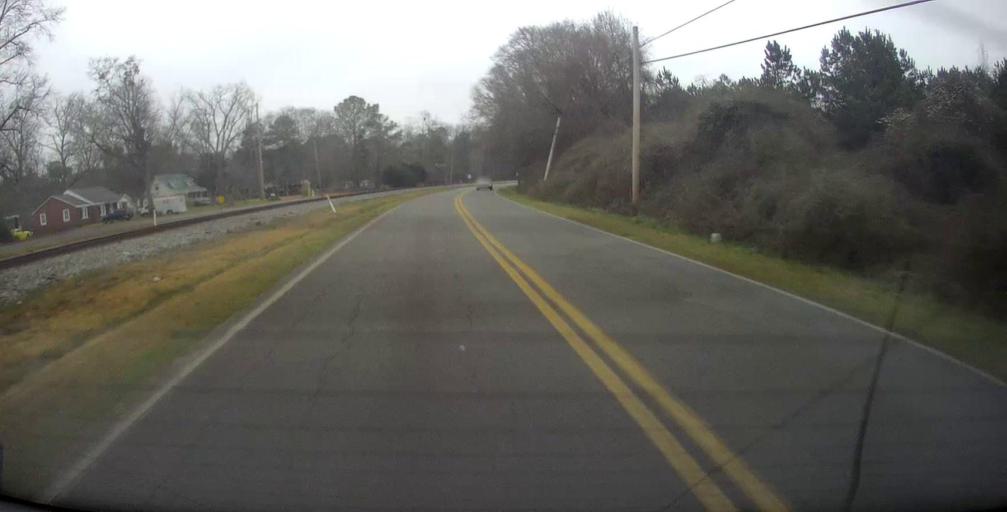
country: US
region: Georgia
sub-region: Lamar County
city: Barnesville
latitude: 33.1230
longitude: -84.1959
